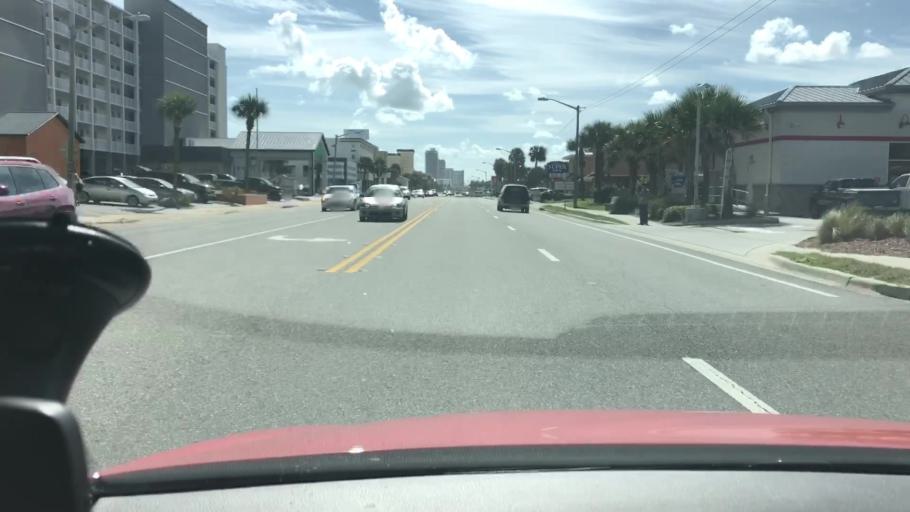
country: US
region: Florida
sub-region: Volusia County
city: Ormond Beach
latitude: 29.2803
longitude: -81.0343
